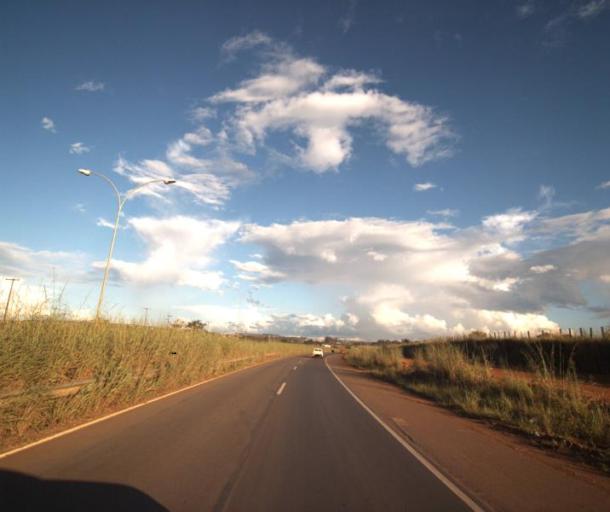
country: BR
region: Goias
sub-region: Anapolis
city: Anapolis
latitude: -16.3000
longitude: -48.9270
